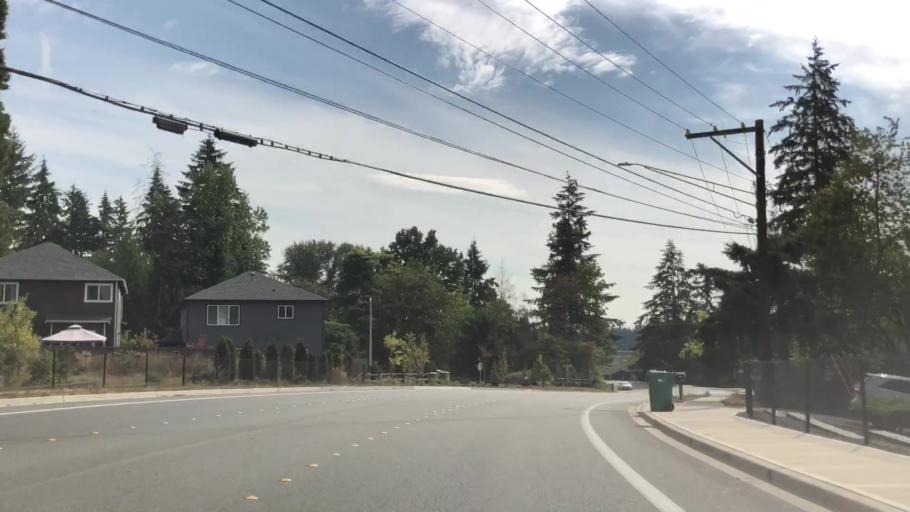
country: US
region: Washington
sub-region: Snohomish County
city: Martha Lake
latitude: 47.8387
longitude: -122.2357
